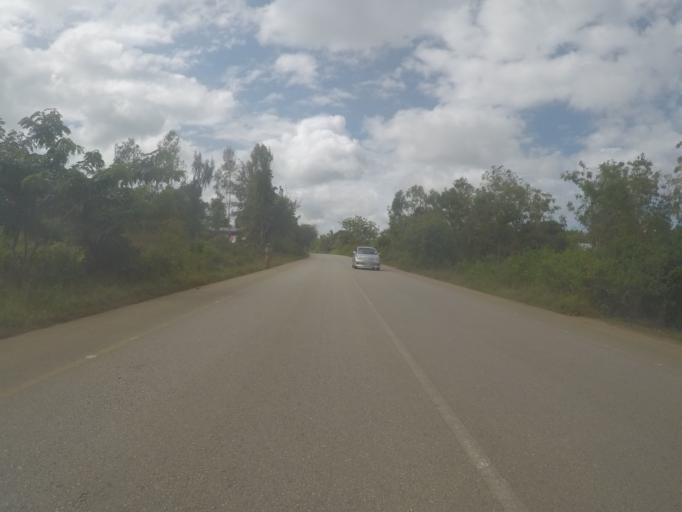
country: TZ
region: Zanzibar North
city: Kijini
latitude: -5.8503
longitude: 39.2832
